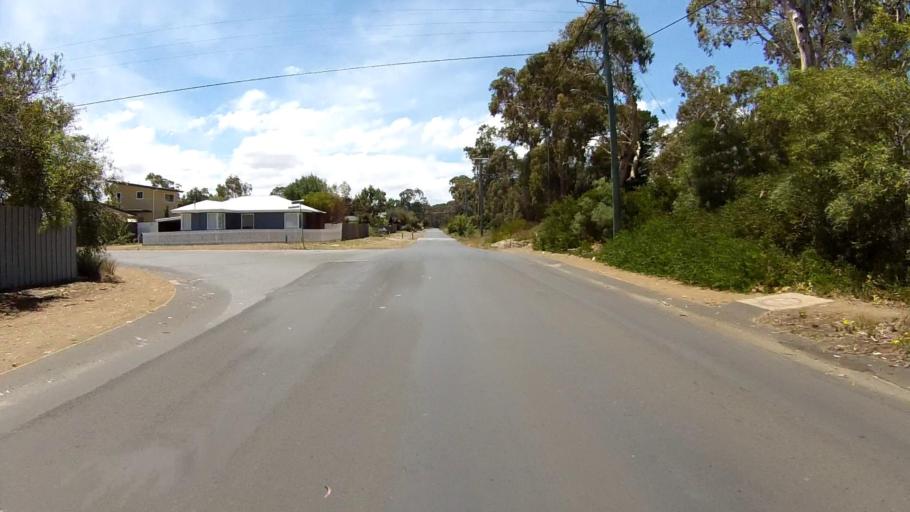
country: AU
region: Tasmania
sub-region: Clarence
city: Seven Mile Beach
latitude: -42.8587
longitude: 147.5079
